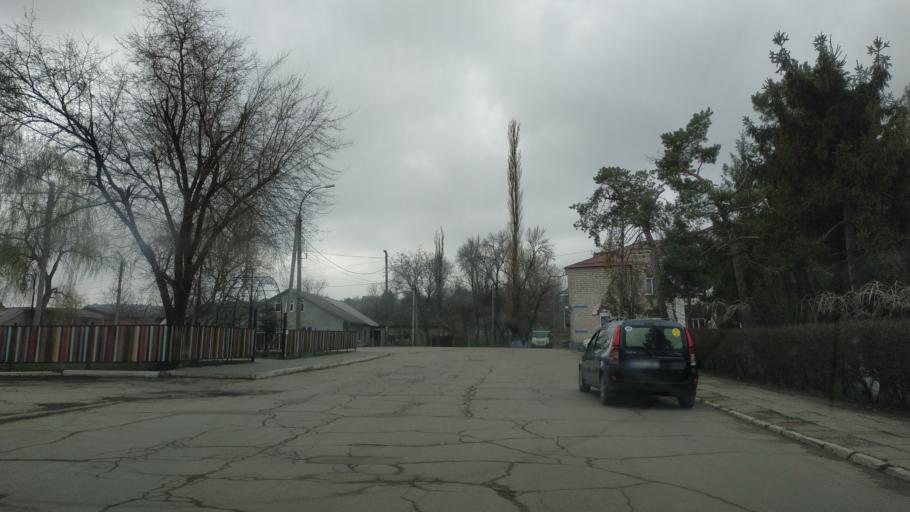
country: MD
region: Cimislia
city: Cimislia
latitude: 46.5207
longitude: 28.7836
